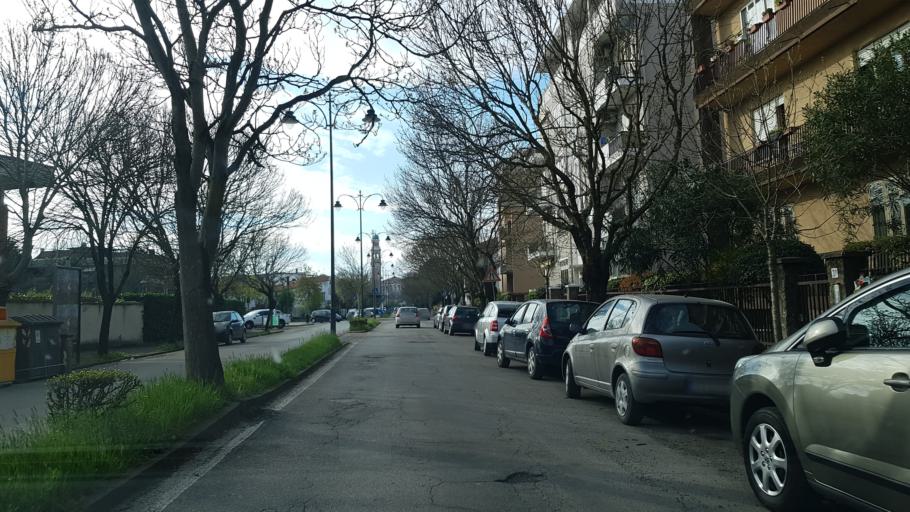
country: IT
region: Veneto
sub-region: Provincia di Rovigo
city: Rovigo
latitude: 45.0776
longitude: 11.7912
